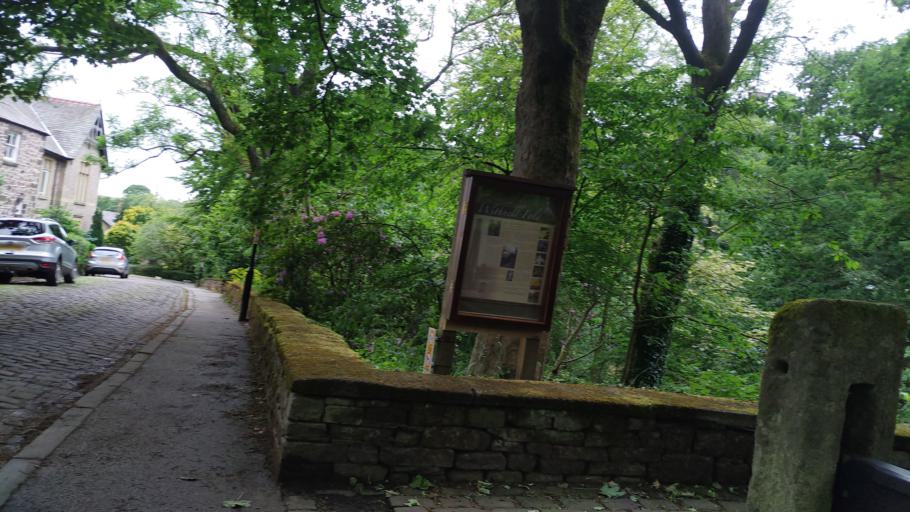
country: GB
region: England
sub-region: Lancashire
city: Chorley
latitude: 53.7027
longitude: -2.5890
